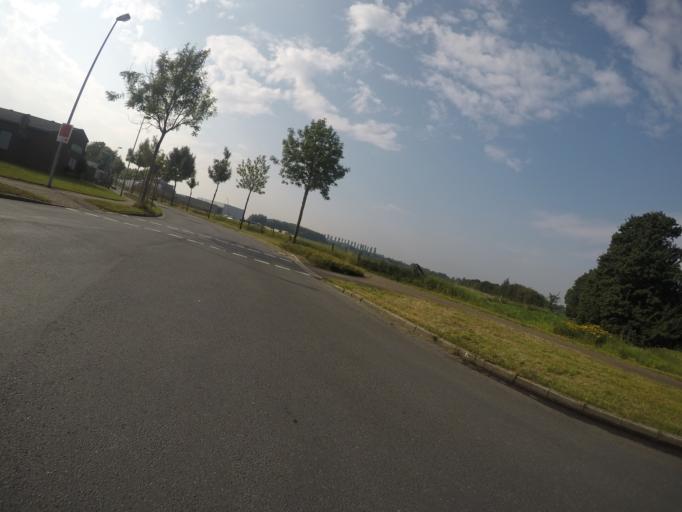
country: DE
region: North Rhine-Westphalia
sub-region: Regierungsbezirk Munster
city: Isselburg
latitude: 51.8154
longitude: 6.5384
